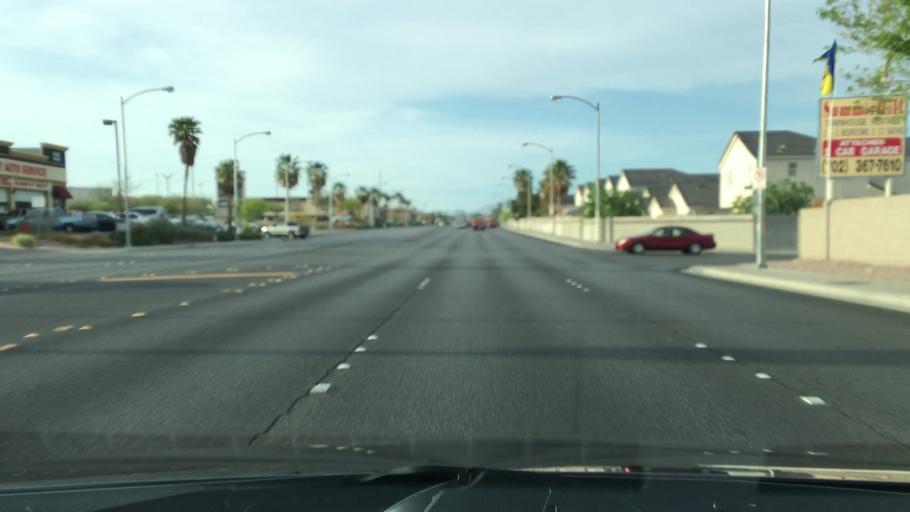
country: US
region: Nevada
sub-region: Clark County
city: Summerlin South
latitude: 36.1109
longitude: -115.2971
